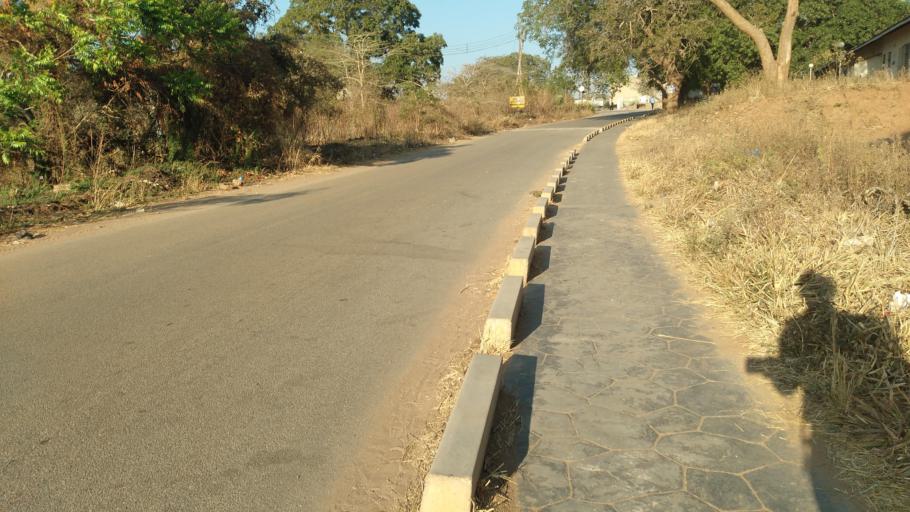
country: ZM
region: Lusaka
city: Lusaka
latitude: -15.5472
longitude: 28.2742
